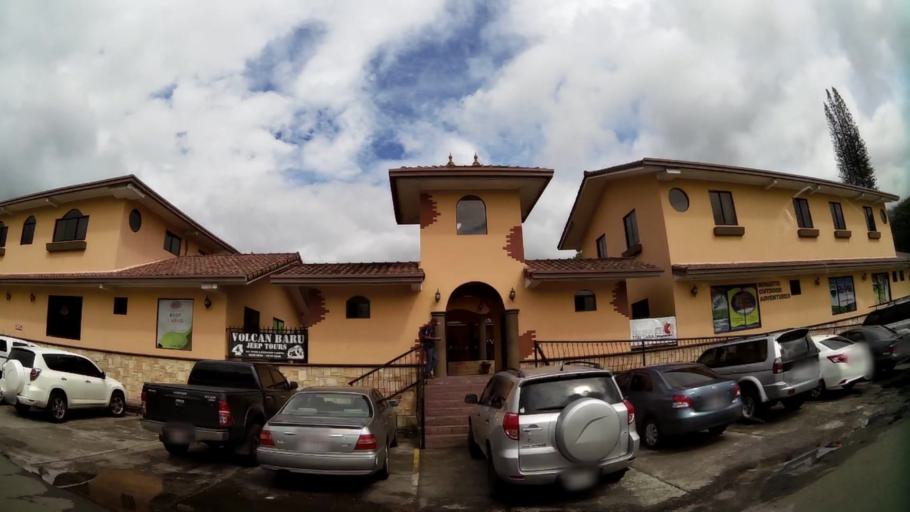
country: PA
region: Chiriqui
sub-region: Distrito Boquete
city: Boquete
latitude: 8.7751
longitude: -82.4330
